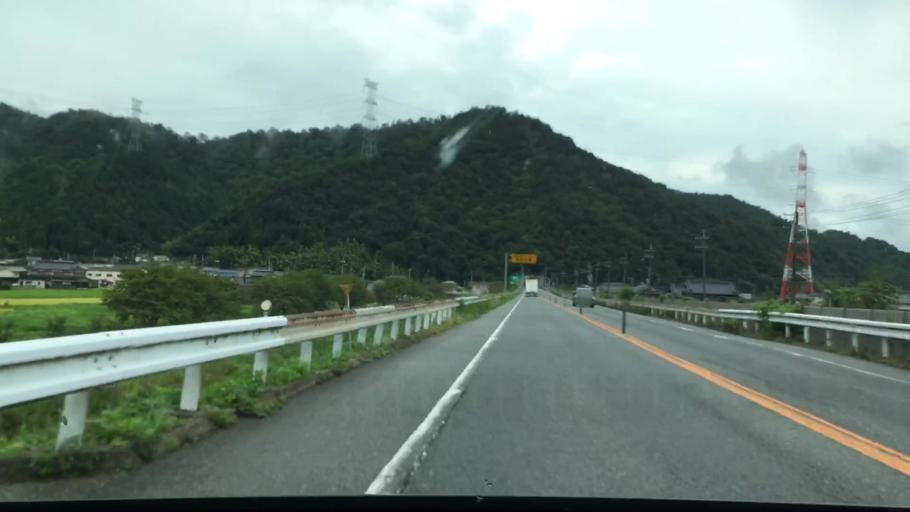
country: JP
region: Hyogo
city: Himeji
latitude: 34.9754
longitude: 134.7688
